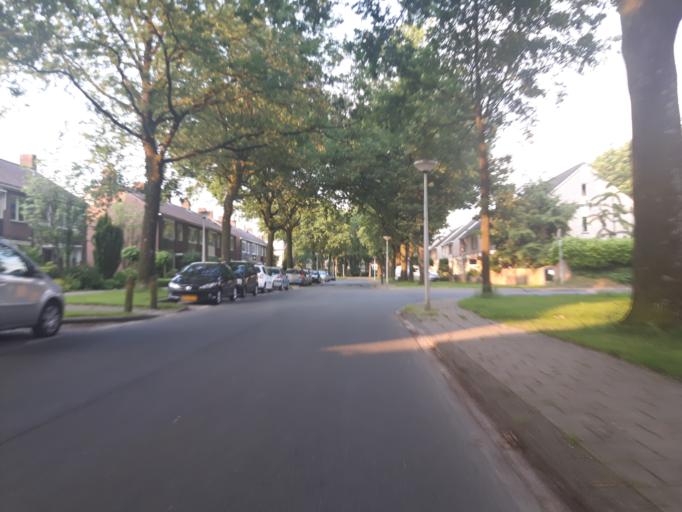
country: NL
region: Overijssel
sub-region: Gemeente Enschede
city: Enschede
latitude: 52.2139
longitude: 6.8511
